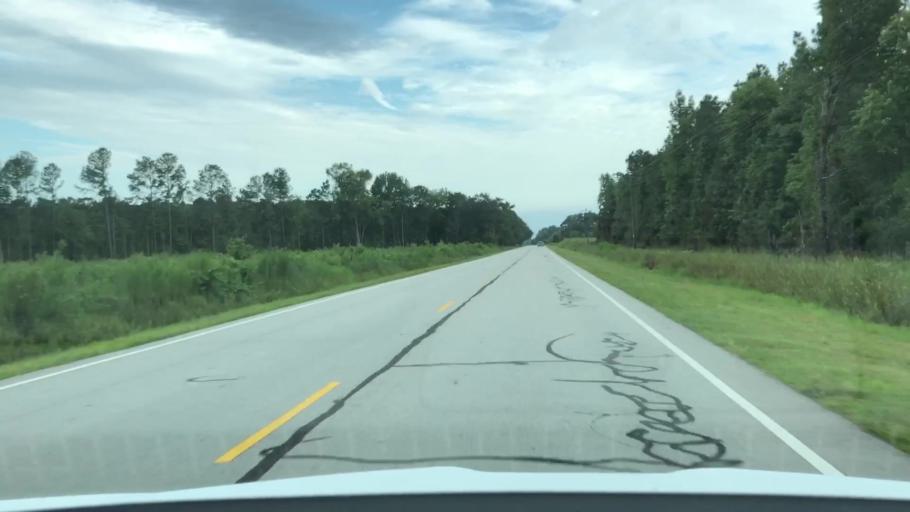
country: US
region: North Carolina
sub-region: Lenoir County
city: Kinston
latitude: 35.1299
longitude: -77.5235
